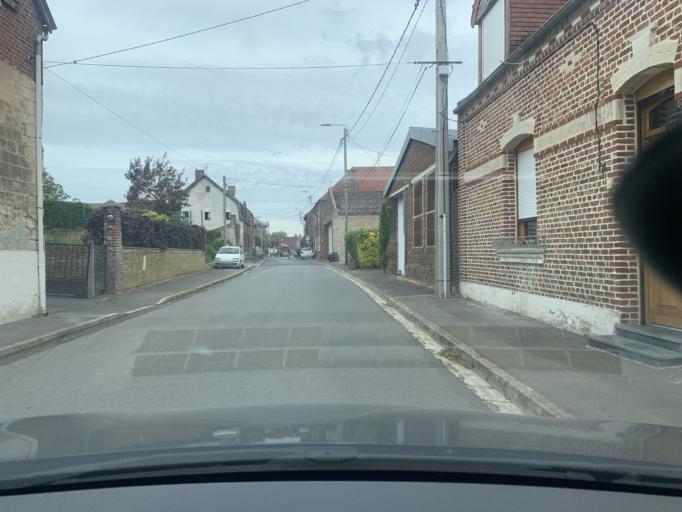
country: FR
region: Nord-Pas-de-Calais
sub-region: Departement du Nord
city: Marcoing
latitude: 50.1392
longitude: 3.1820
